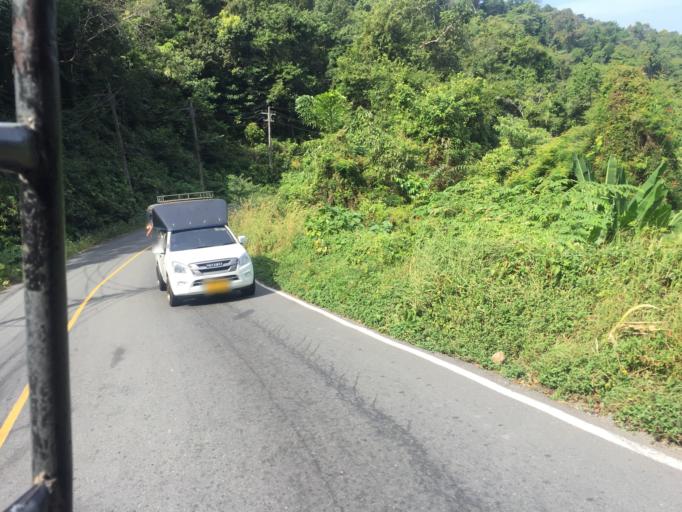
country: TH
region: Trat
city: Laem Ngop
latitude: 12.1233
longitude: 102.2685
